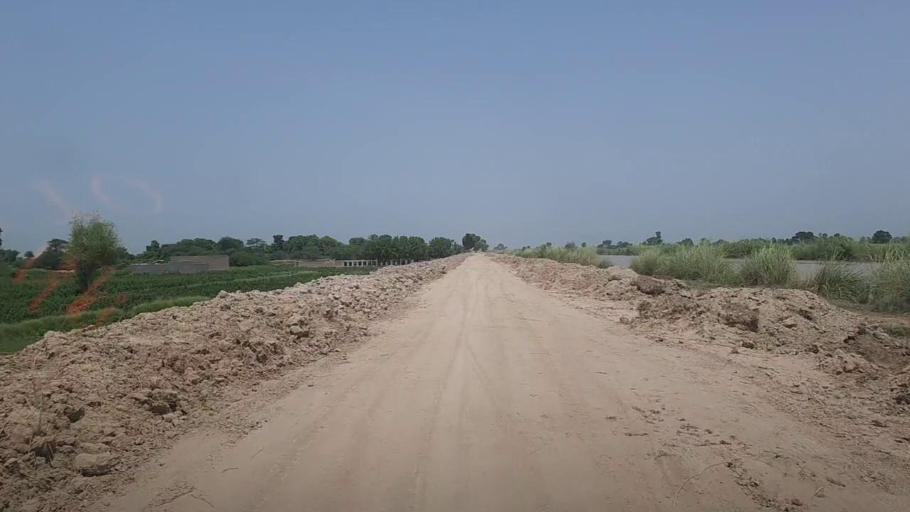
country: PK
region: Sindh
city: Pad Idan
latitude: 26.7887
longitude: 68.2766
